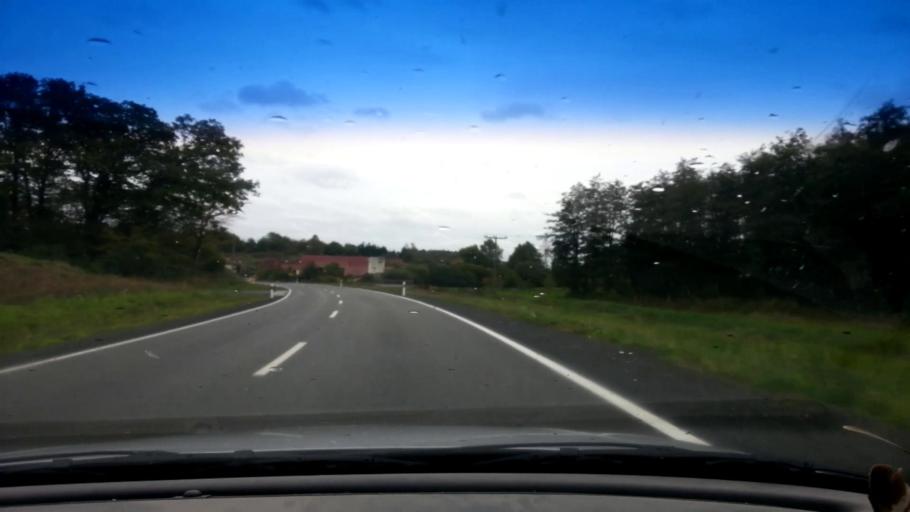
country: DE
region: Bavaria
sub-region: Regierungsbezirk Unterfranken
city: Stettfeld
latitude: 50.0047
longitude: 10.7415
